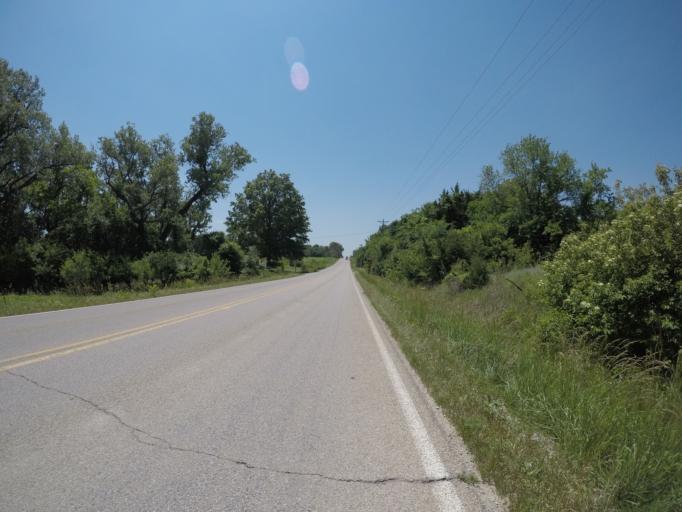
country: US
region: Kansas
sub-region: Riley County
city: Manhattan
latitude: 39.2423
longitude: -96.4453
